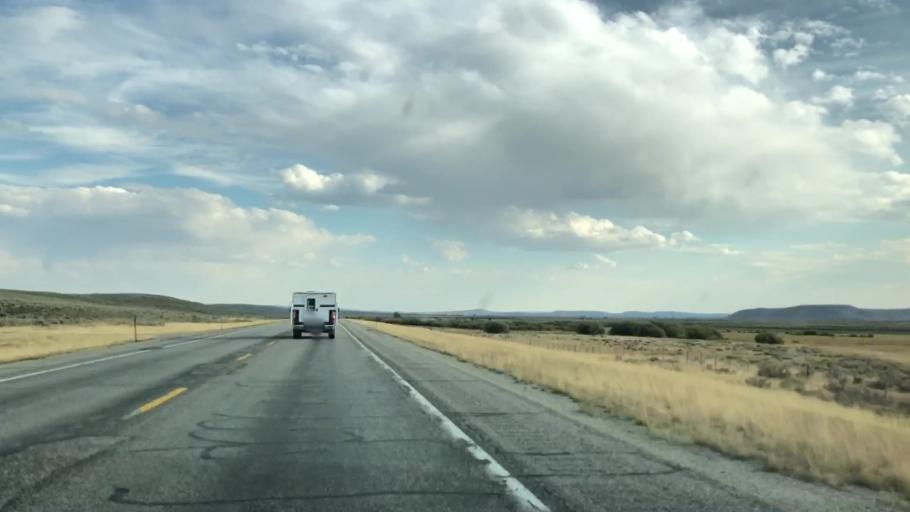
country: US
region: Wyoming
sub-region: Sublette County
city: Pinedale
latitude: 43.0271
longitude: -110.1253
